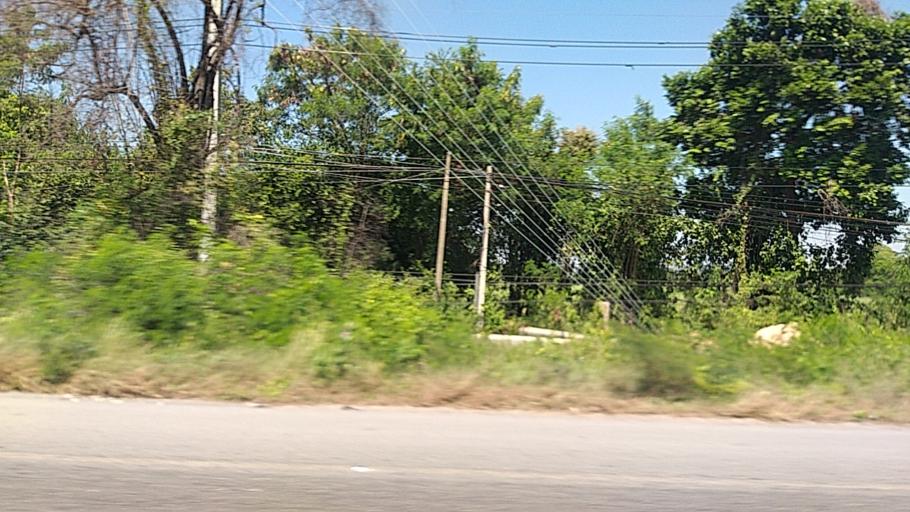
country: TH
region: Nakhon Ratchasima
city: Amphoe Sikhiu
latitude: 14.8608
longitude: 101.6910
